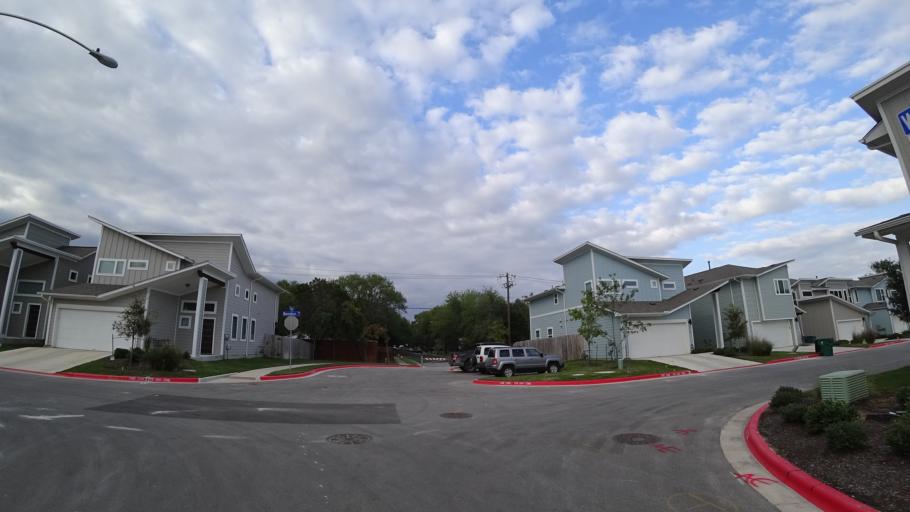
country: US
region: Texas
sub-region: Travis County
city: Onion Creek
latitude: 30.1901
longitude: -97.7924
